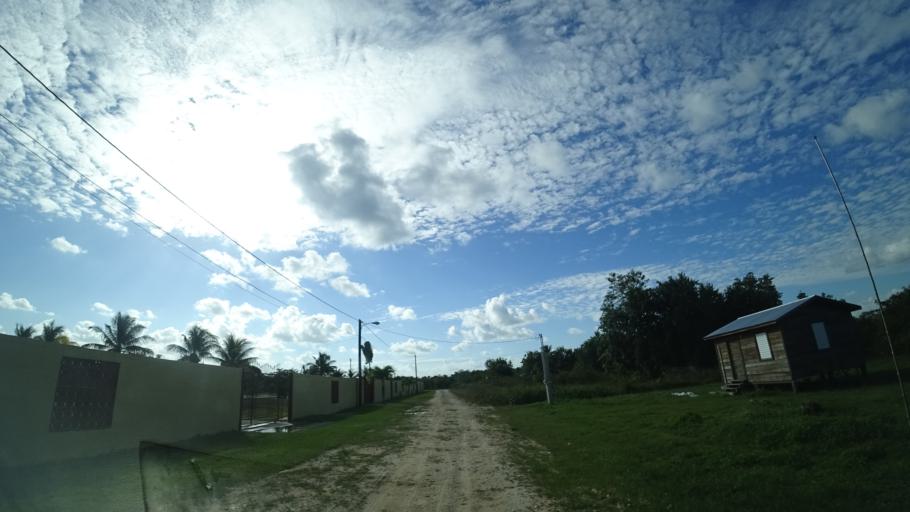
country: BZ
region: Belize
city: Belize City
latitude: 17.5552
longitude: -88.4007
